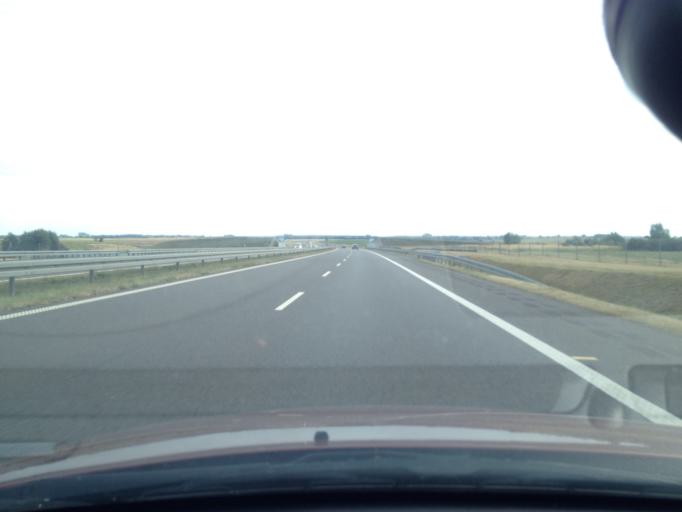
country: PL
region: West Pomeranian Voivodeship
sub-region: Powiat pyrzycki
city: Bielice
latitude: 53.1409
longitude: 14.7193
